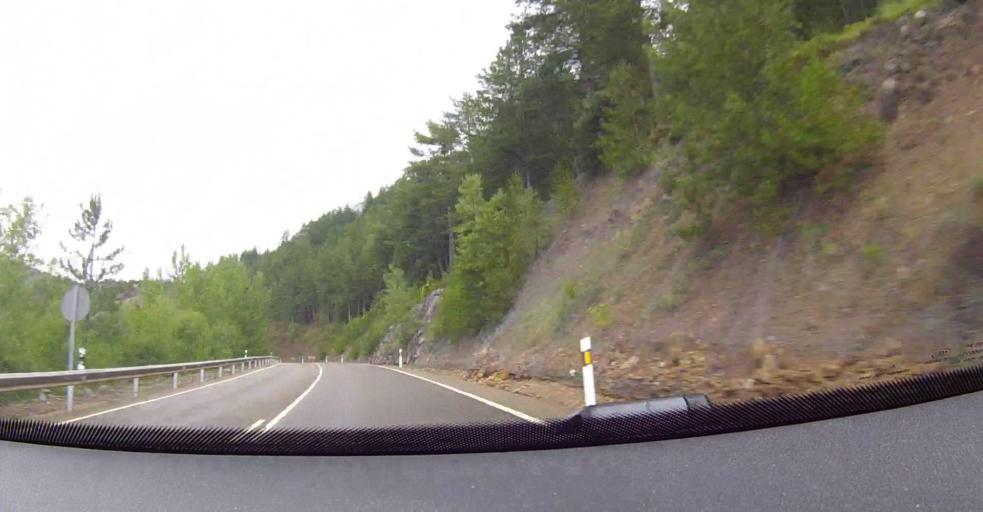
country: ES
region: Castille and Leon
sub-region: Provincia de Leon
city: Cistierna
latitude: 42.8228
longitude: -5.1198
